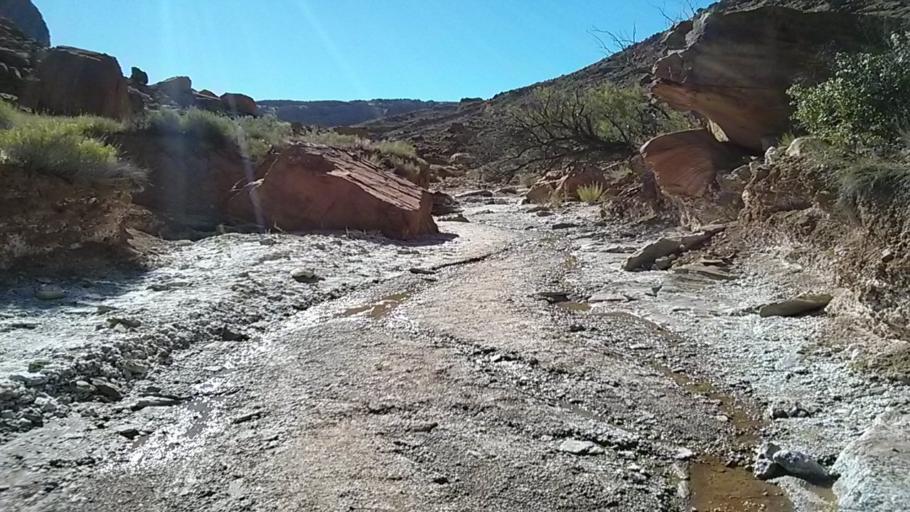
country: US
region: Utah
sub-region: Grand County
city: Moab
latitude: 38.4418
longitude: -109.9462
